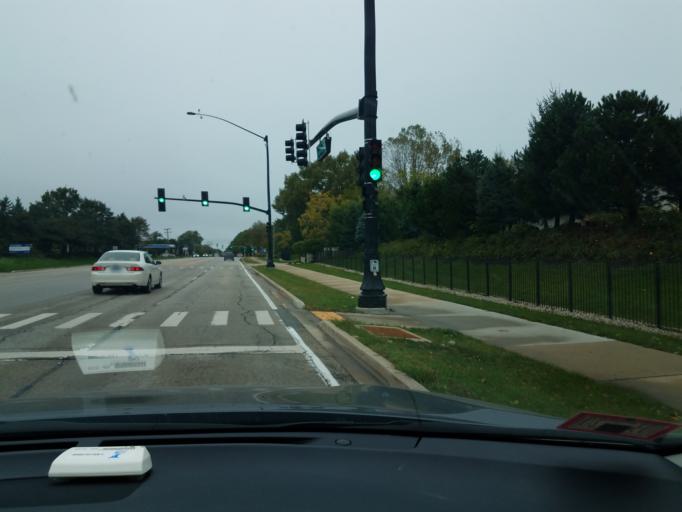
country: US
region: Illinois
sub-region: Lake County
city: Riverwoods
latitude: 42.1676
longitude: -87.8793
